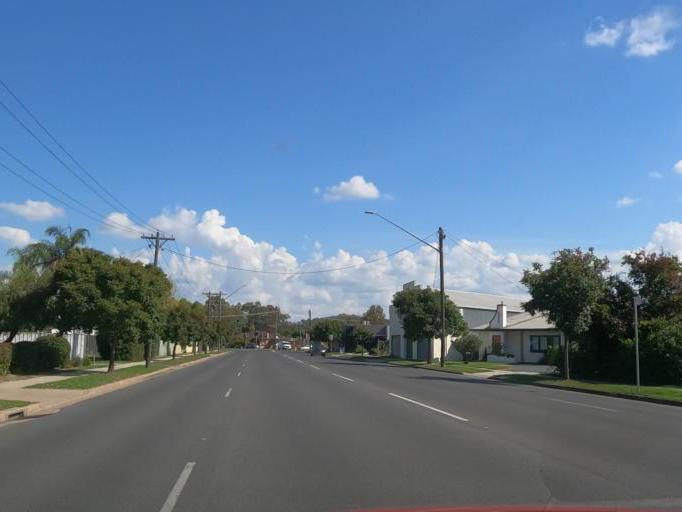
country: AU
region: New South Wales
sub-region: Albury Municipality
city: North Albury
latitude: -36.0560
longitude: 146.9284
